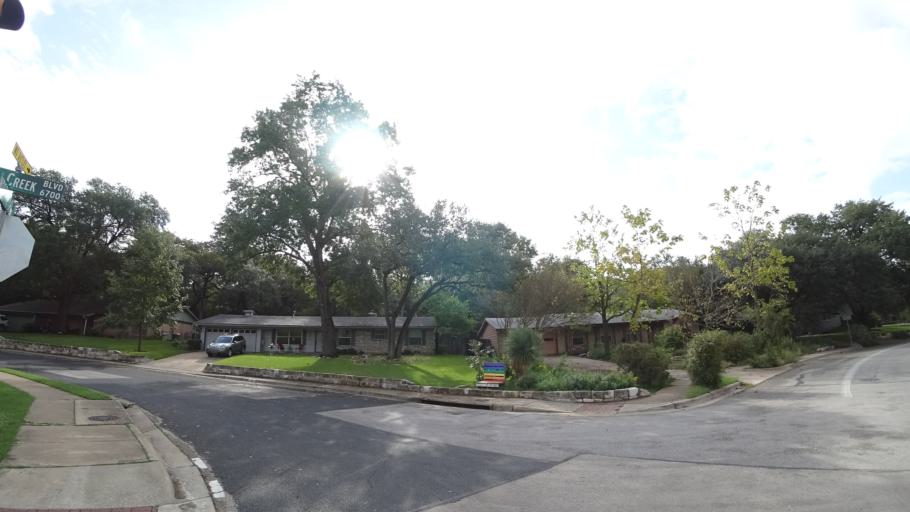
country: US
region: Texas
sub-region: Travis County
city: West Lake Hills
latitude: 30.3460
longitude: -97.7451
